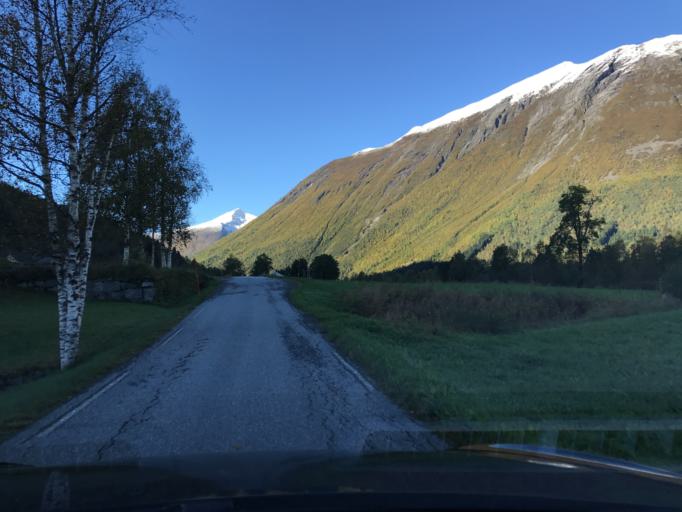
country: NO
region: More og Romsdal
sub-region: Norddal
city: Valldal
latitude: 62.3304
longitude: 7.3632
